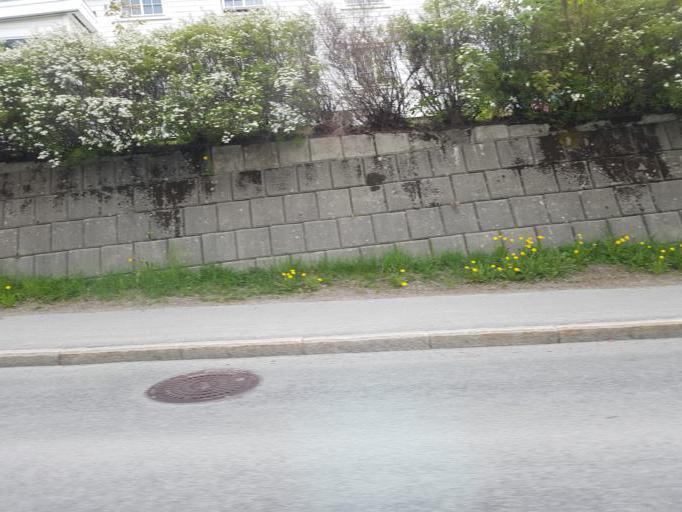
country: NO
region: Nord-Trondelag
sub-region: Levanger
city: Levanger
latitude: 63.7478
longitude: 11.2768
